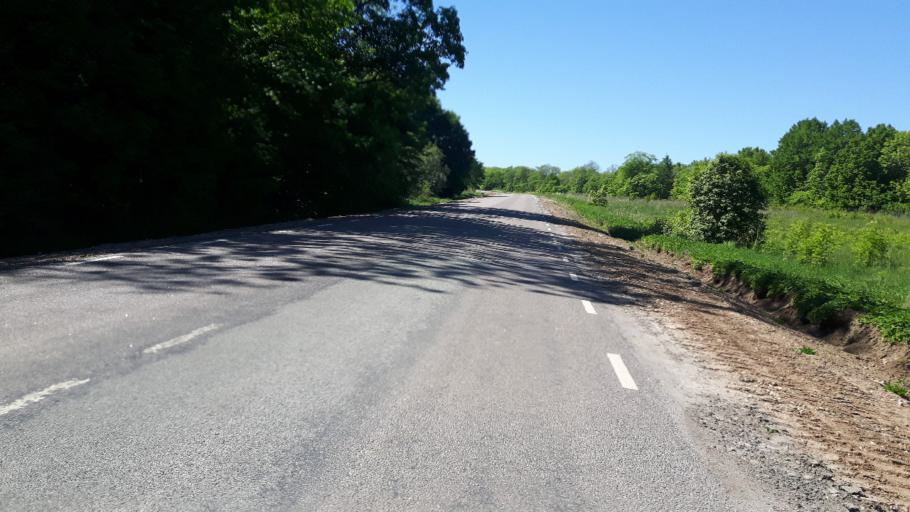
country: EE
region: Ida-Virumaa
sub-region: Narva-Joesuu linn
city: Narva-Joesuu
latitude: 59.4113
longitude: 27.9502
